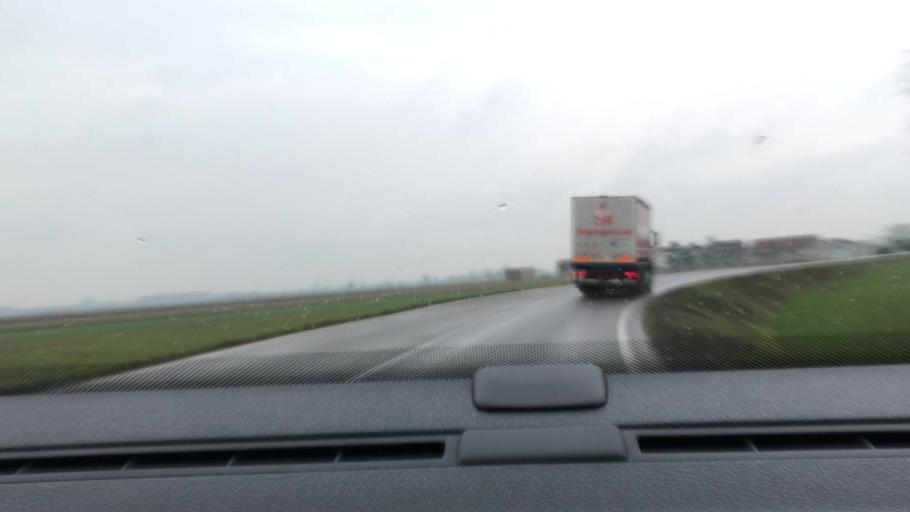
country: IT
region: Lombardy
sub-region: Provincia di Mantova
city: Gazzuolo
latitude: 45.0091
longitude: 10.6044
